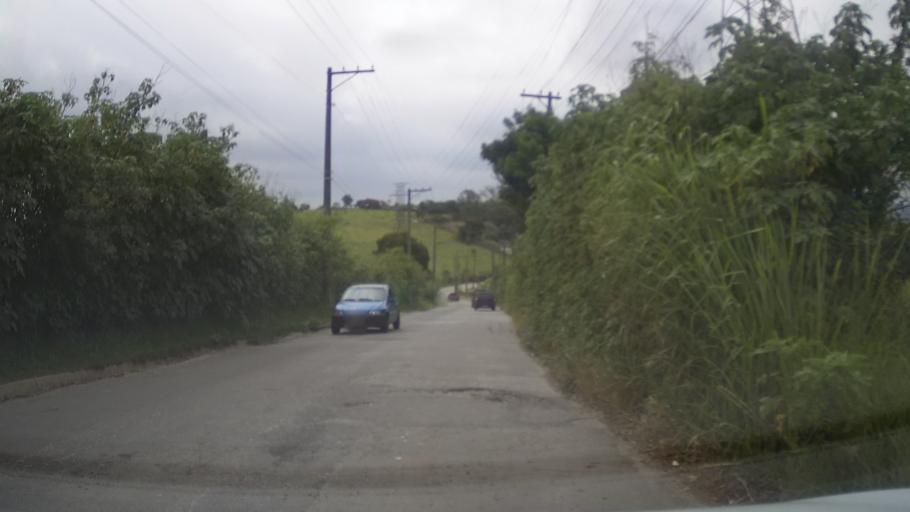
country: BR
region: Sao Paulo
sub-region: Itaquaquecetuba
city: Itaquaquecetuba
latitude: -23.4480
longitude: -46.3913
